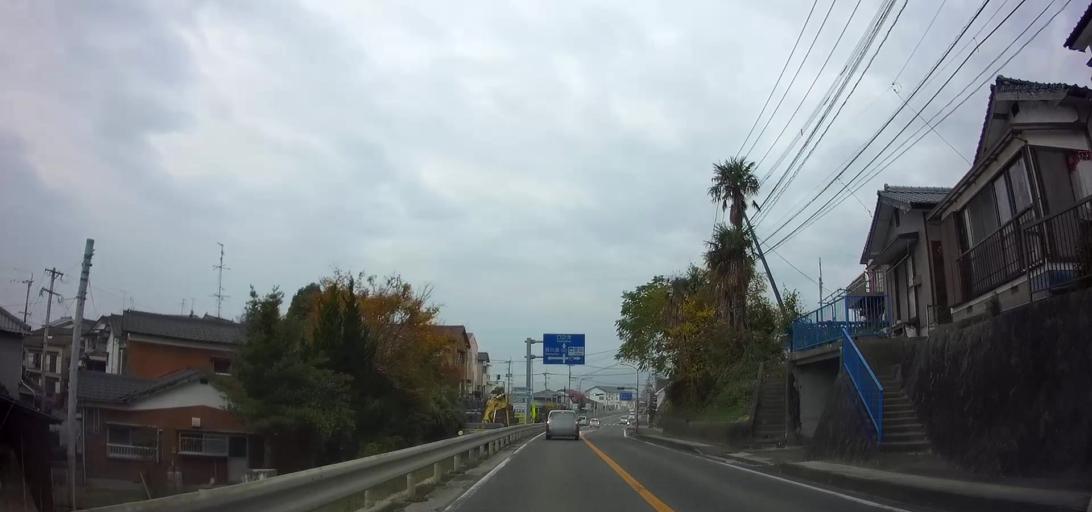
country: JP
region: Nagasaki
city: Shimabara
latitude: 32.6546
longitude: 130.2898
